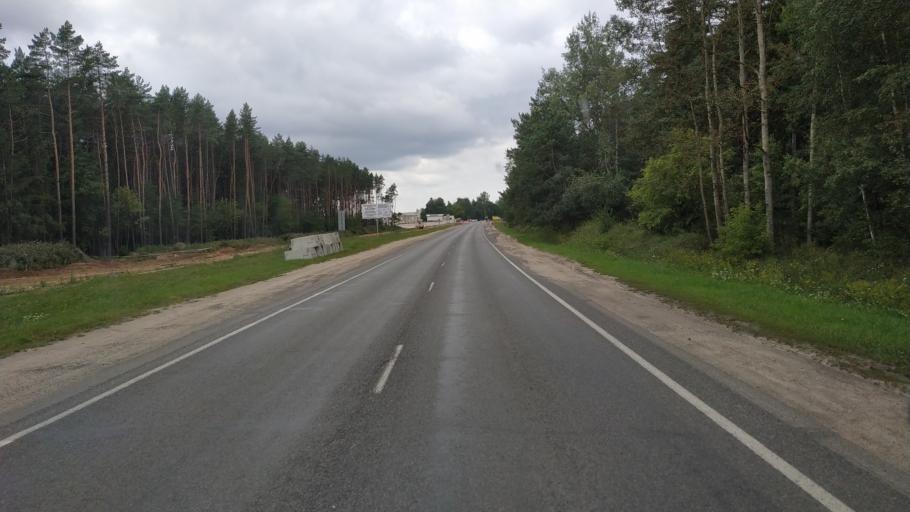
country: BY
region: Mogilev
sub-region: Mahilyowski Rayon
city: Veyno
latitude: 53.8782
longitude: 30.4152
